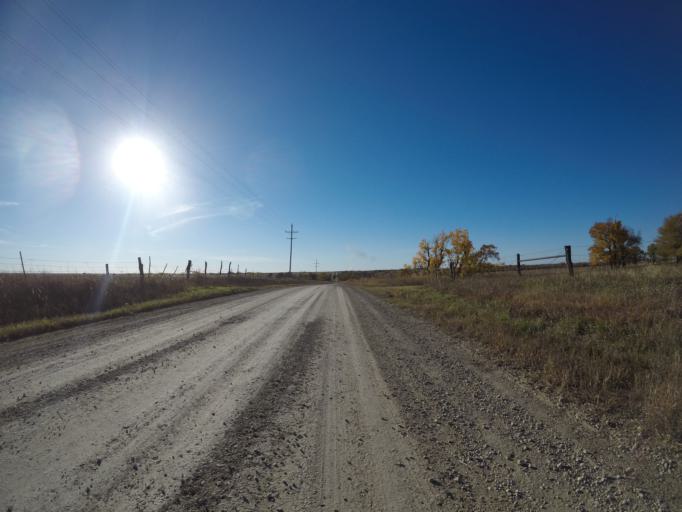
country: US
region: Kansas
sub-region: Riley County
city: Ogden
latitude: 39.2616
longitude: -96.7315
